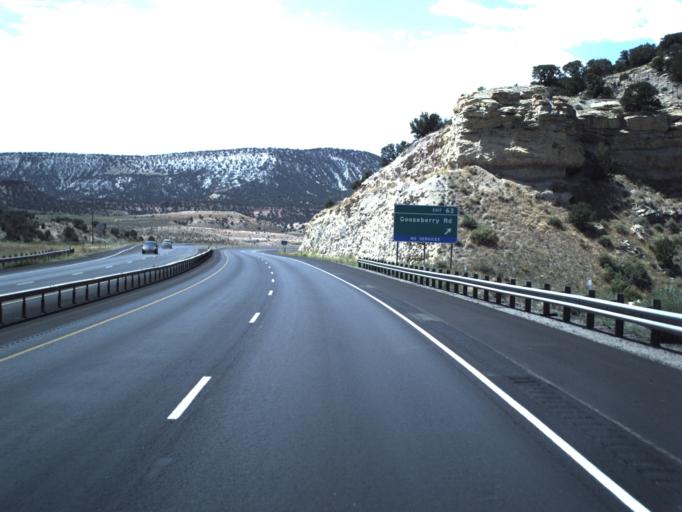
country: US
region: Utah
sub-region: Sevier County
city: Salina
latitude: 38.9165
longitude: -111.7309
